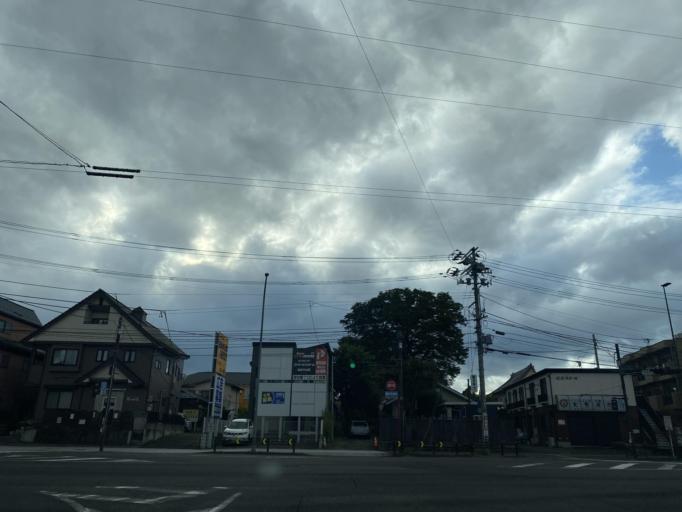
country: JP
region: Miyagi
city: Sendai-shi
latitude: 38.2784
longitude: 140.8607
